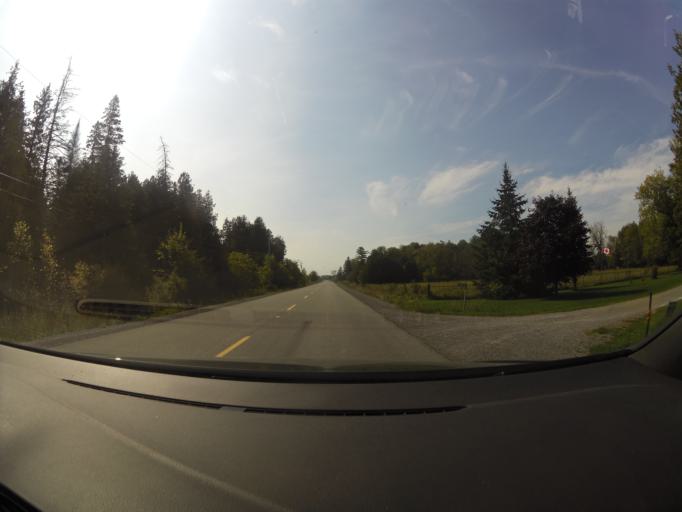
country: CA
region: Ontario
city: Carleton Place
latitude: 45.3223
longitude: -76.1793
